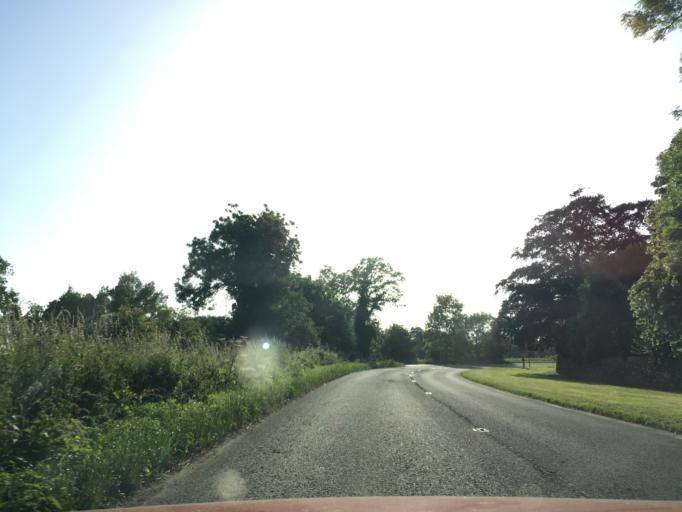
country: GB
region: England
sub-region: Wiltshire
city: Cricklade
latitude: 51.7108
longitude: -1.8861
